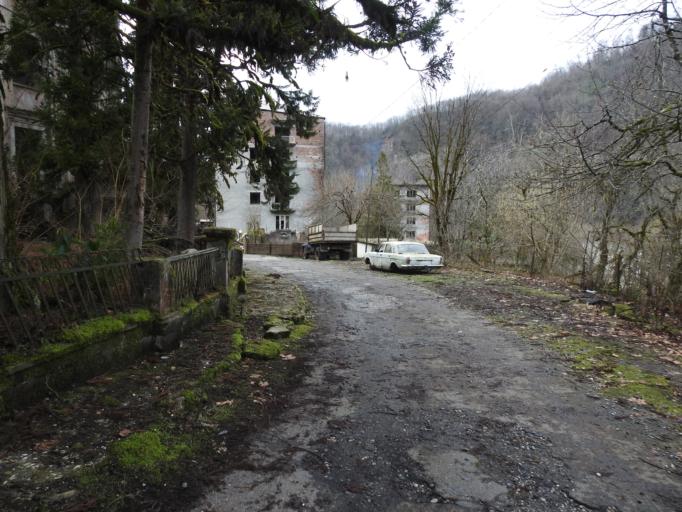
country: GE
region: Abkhazia
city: Tqvarch'eli
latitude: 42.8590
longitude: 41.7724
